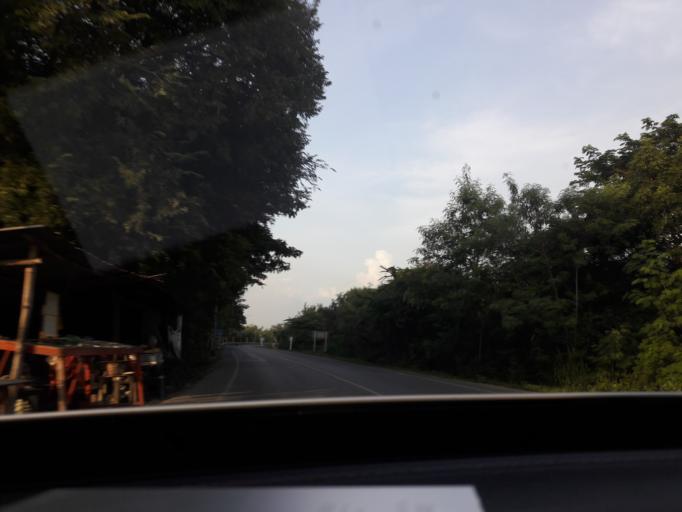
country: TH
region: Ang Thong
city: Pho Thong
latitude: 14.7098
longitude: 100.4282
